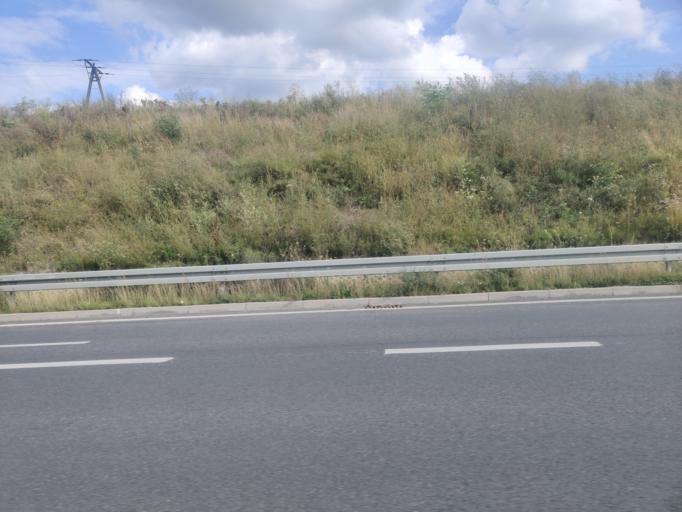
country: PL
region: Greater Poland Voivodeship
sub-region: Konin
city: Konin
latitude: 52.2010
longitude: 18.2713
